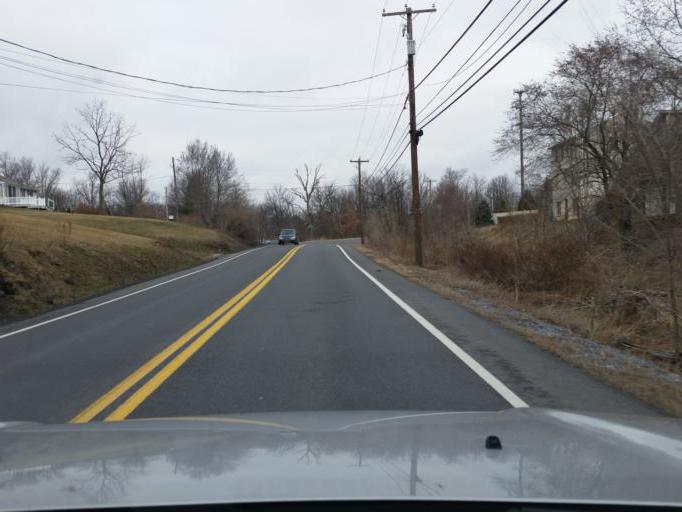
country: US
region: Pennsylvania
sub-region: Dauphin County
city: Paxtonia
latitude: 40.3157
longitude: -76.7777
